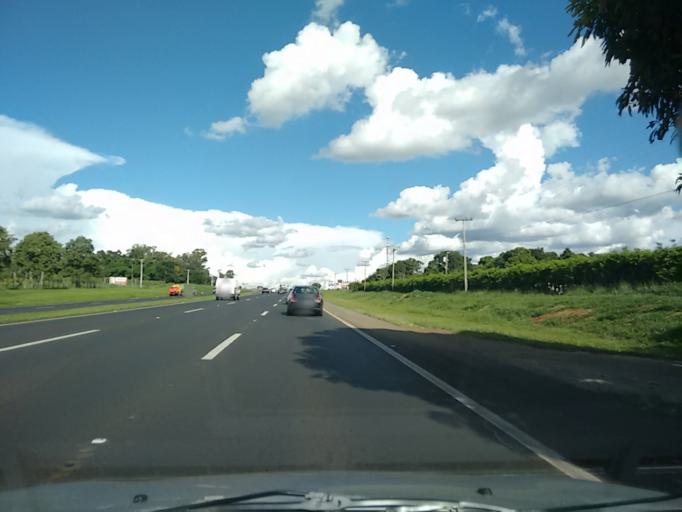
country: BR
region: Sao Paulo
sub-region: Ibate
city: Ibate
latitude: -21.9734
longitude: -47.9425
